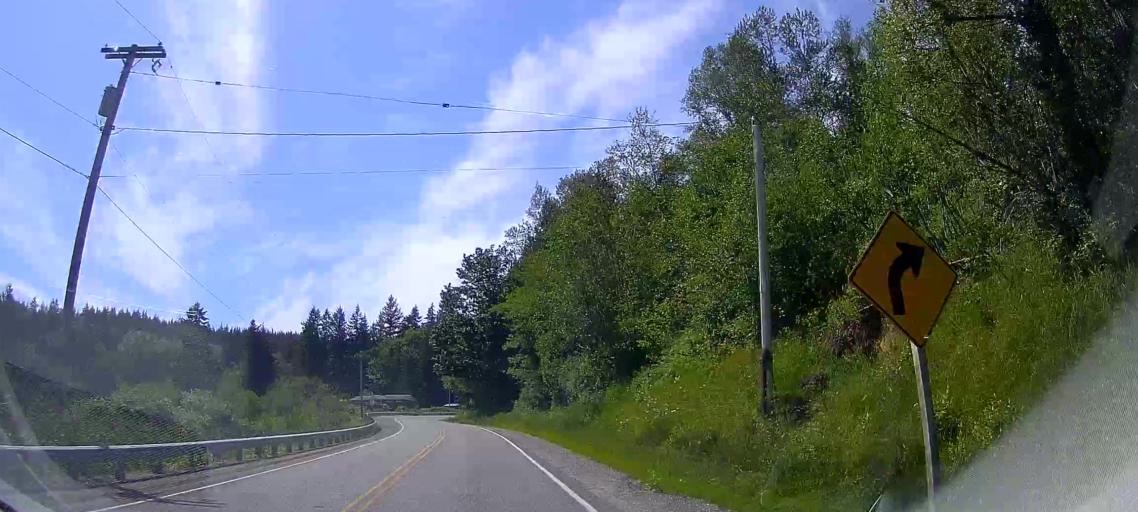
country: US
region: Washington
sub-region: Skagit County
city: Big Lake
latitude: 48.3966
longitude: -122.2889
